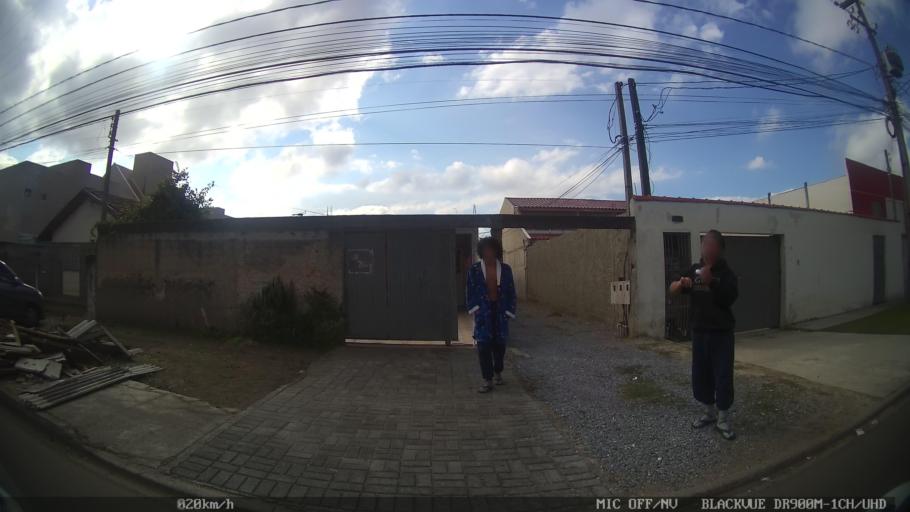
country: BR
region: Parana
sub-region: Pinhais
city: Pinhais
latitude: -25.4039
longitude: -49.1860
